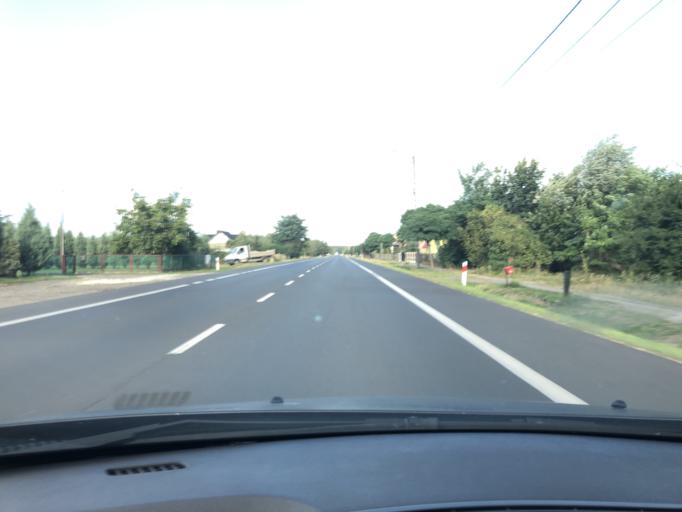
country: PL
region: Lodz Voivodeship
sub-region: Powiat wieruszowski
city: Galewice
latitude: 51.3039
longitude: 18.2528
